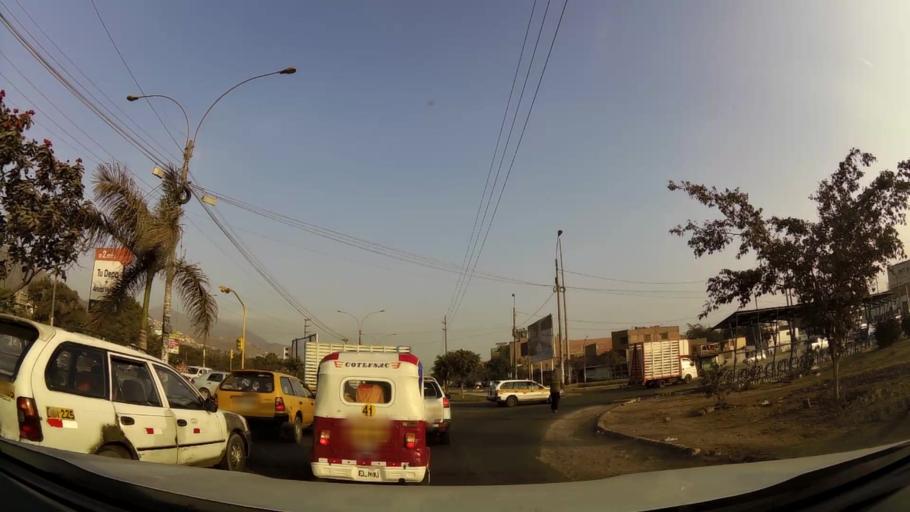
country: PE
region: Lima
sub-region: Lima
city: Independencia
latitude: -11.9612
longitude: -77.0628
